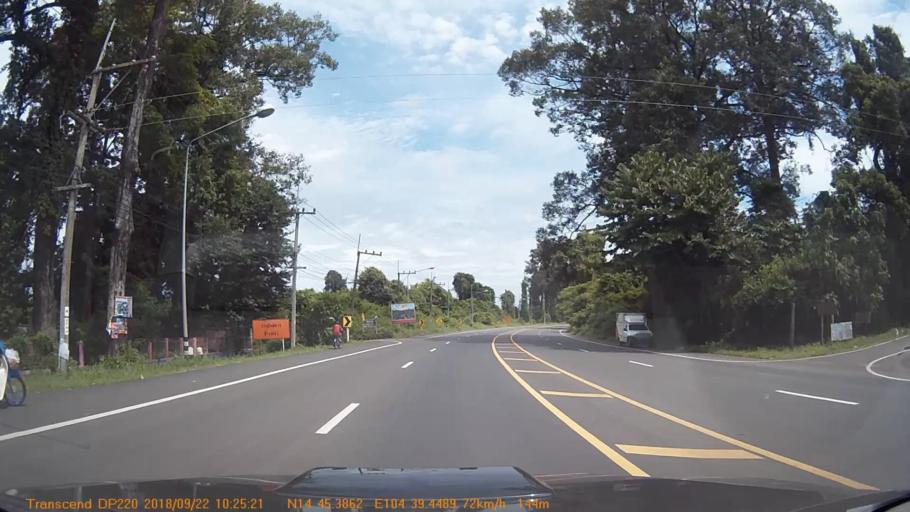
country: TH
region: Sisaket
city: Benchalak
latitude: 14.7565
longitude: 104.6575
